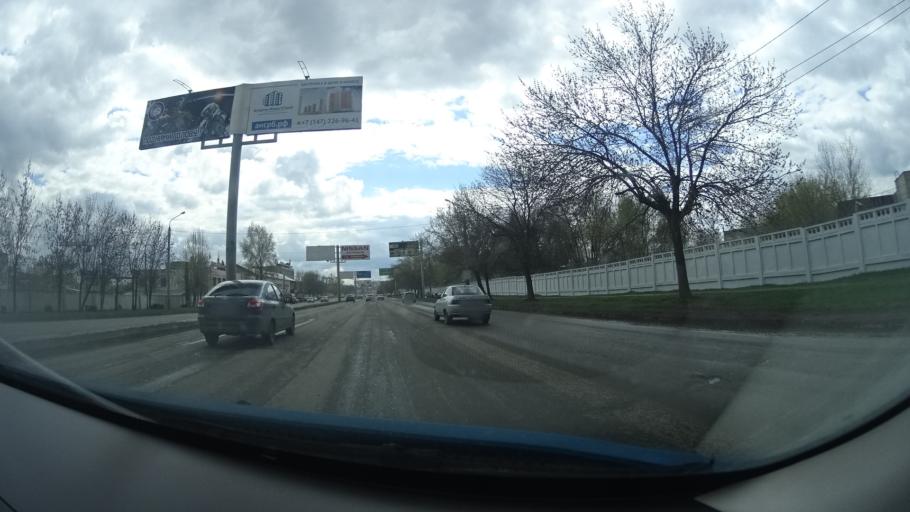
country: RU
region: Bashkortostan
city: Ufa
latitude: 54.8030
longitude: 56.0808
